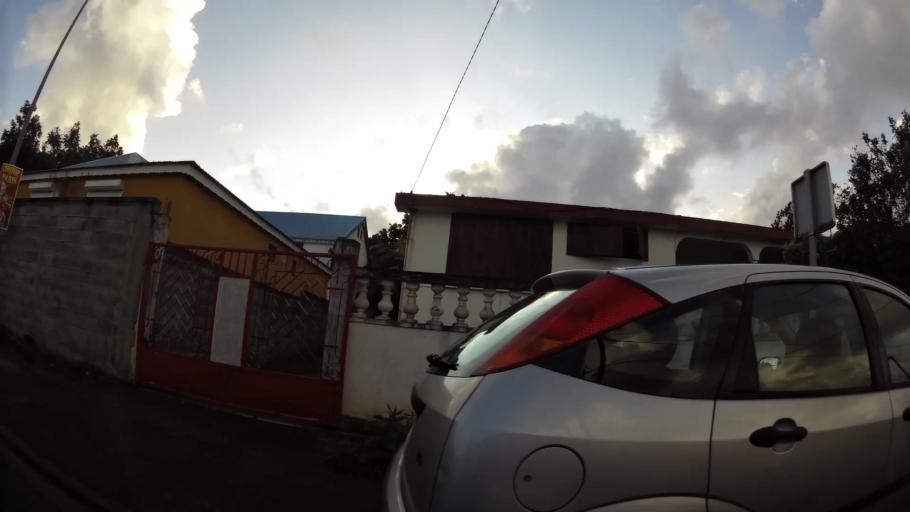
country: GP
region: Guadeloupe
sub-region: Guadeloupe
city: Petit-Bourg
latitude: 16.1358
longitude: -61.5763
